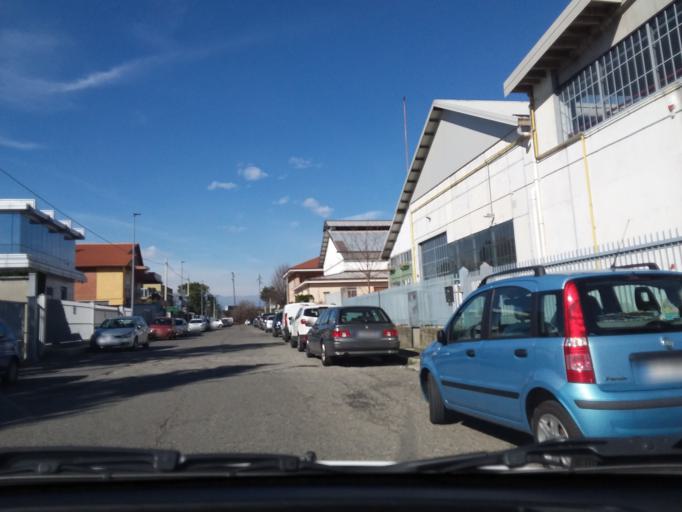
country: IT
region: Piedmont
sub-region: Provincia di Torino
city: Collegno
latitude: 45.0801
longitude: 7.5567
